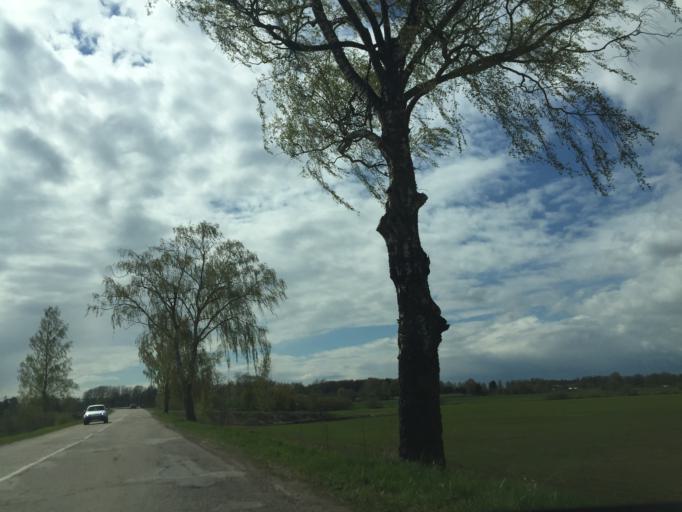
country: LV
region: Rundales
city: Pilsrundale
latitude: 56.5739
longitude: 23.9725
